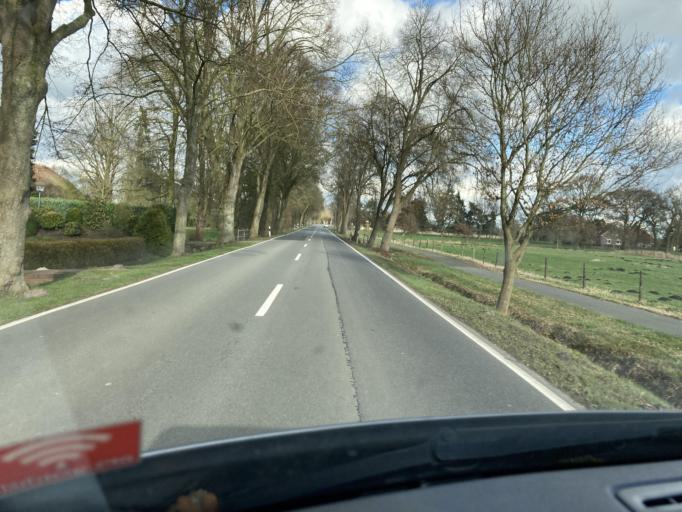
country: DE
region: Lower Saxony
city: Friedeburg
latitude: 53.3668
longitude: 7.8179
